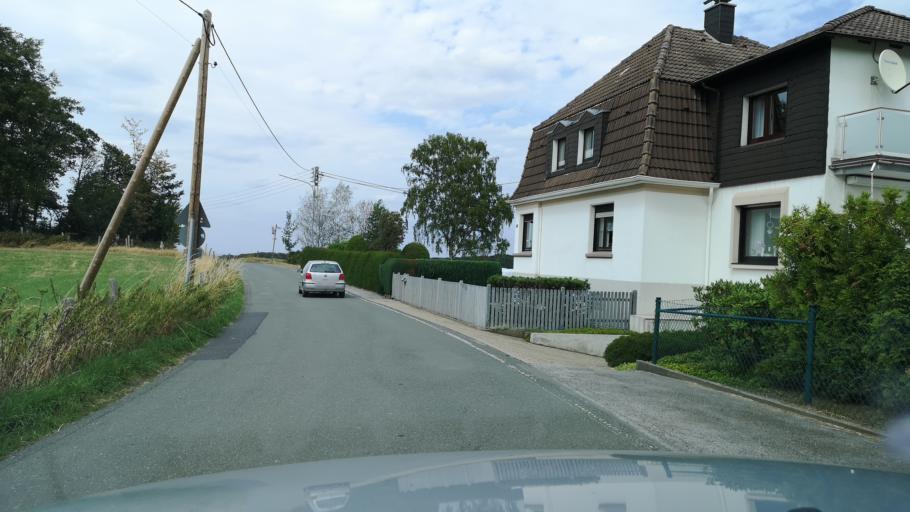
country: DE
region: North Rhine-Westphalia
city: Sprockhovel
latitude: 51.3536
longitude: 7.1982
